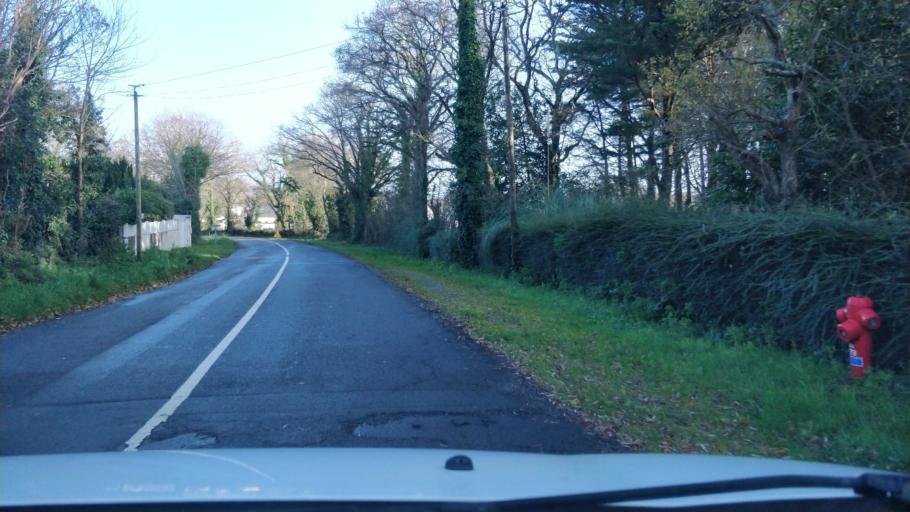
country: FR
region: Pays de la Loire
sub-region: Departement de la Loire-Atlantique
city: Mesquer
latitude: 47.3945
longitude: -2.4651
